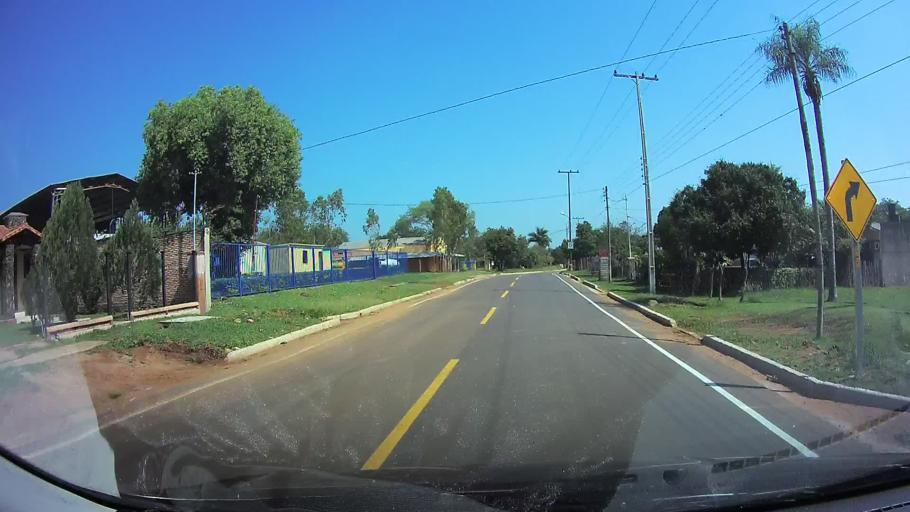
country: PY
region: Central
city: Limpio
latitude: -25.2269
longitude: -57.4888
